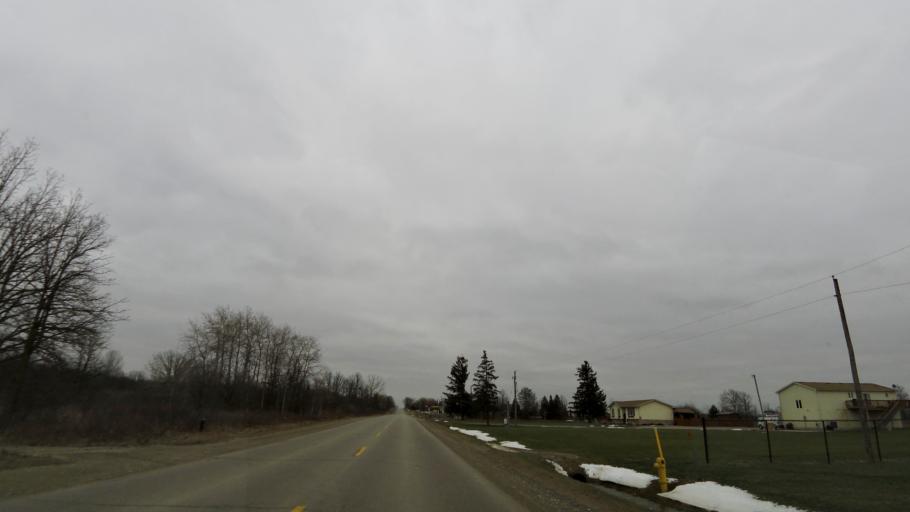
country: CA
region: Ontario
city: Ancaster
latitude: 43.0530
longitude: -80.0756
